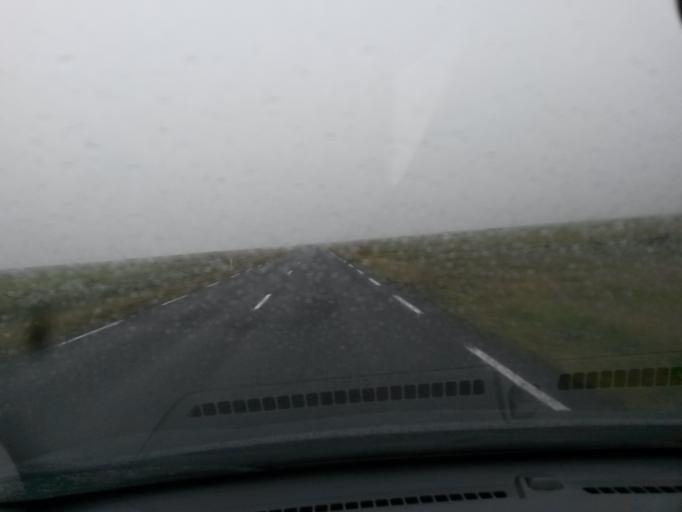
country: IS
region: South
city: Vestmannaeyjar
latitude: 63.4382
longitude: -19.1950
